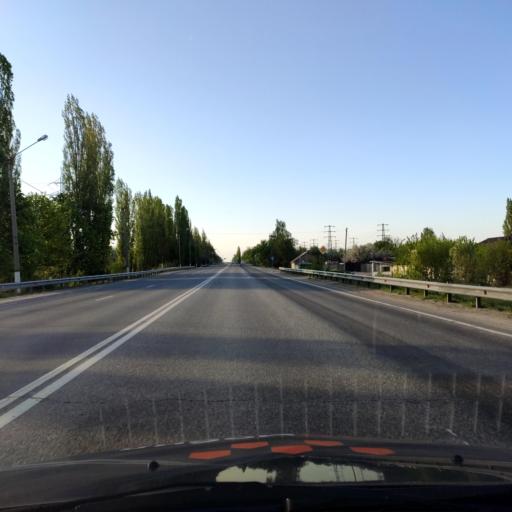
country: RU
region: Lipetsk
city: Yelets
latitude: 52.6056
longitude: 38.4675
